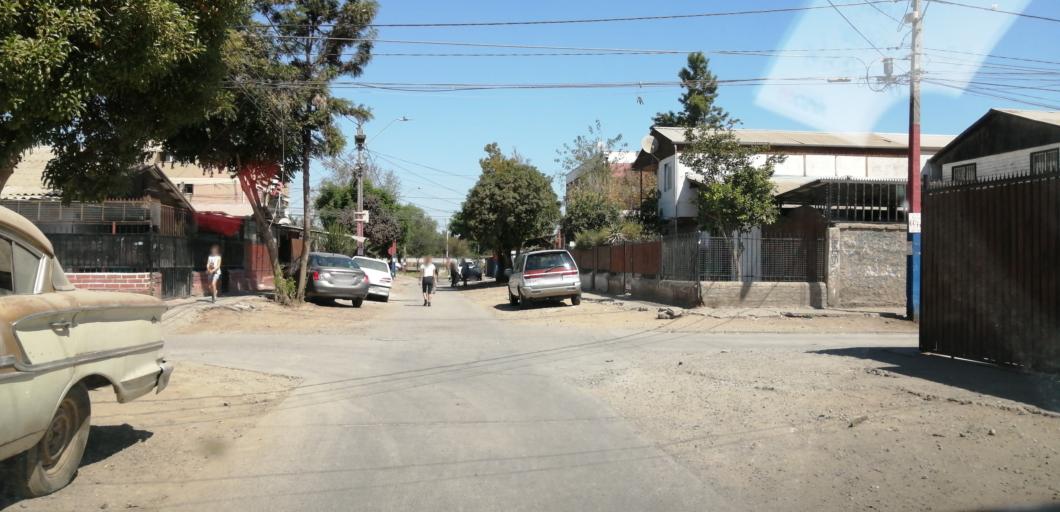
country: CL
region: Santiago Metropolitan
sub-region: Provincia de Santiago
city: Lo Prado
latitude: -33.4488
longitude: -70.7522
